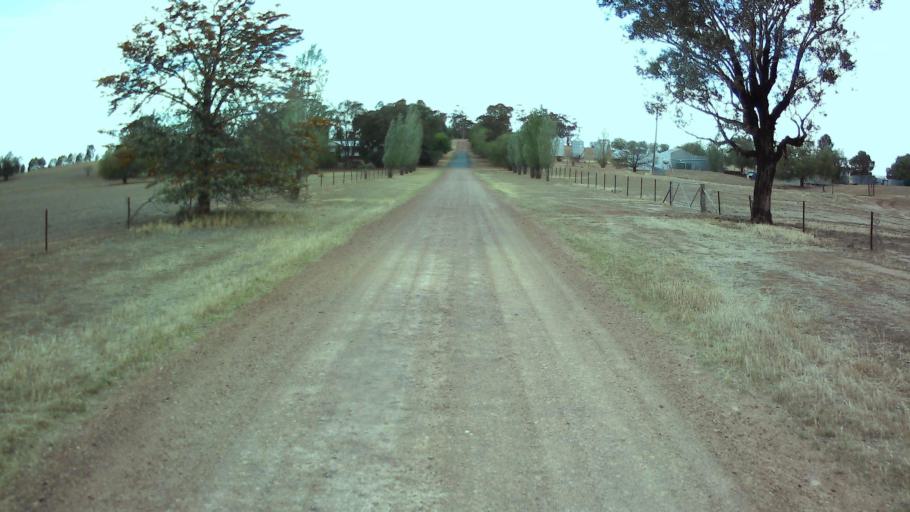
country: AU
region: New South Wales
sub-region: Weddin
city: Grenfell
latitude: -33.9959
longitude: 148.3092
